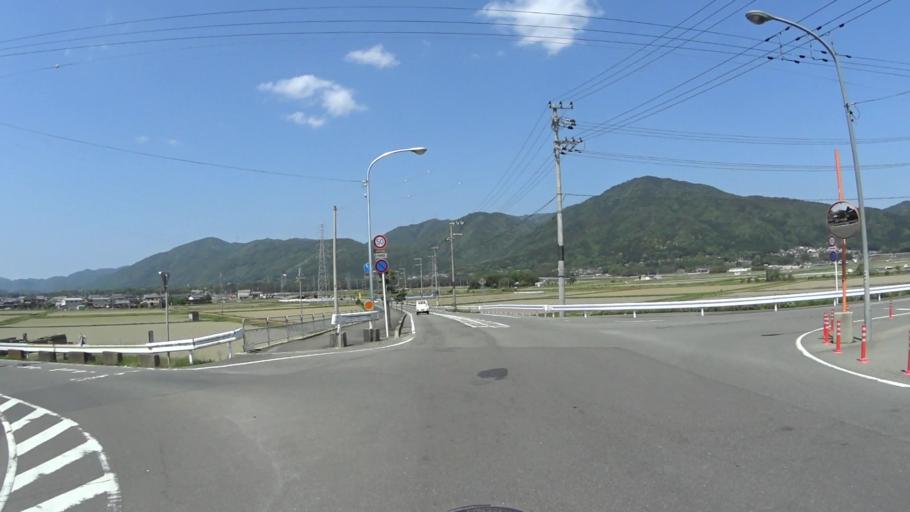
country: JP
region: Kyoto
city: Kameoka
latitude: 35.0283
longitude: 135.5720
